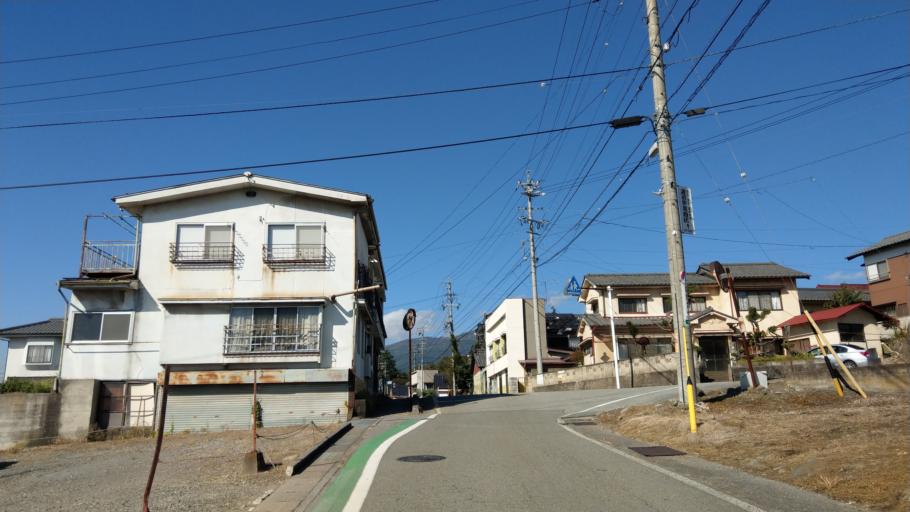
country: JP
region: Nagano
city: Komoro
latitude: 36.3202
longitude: 138.4332
